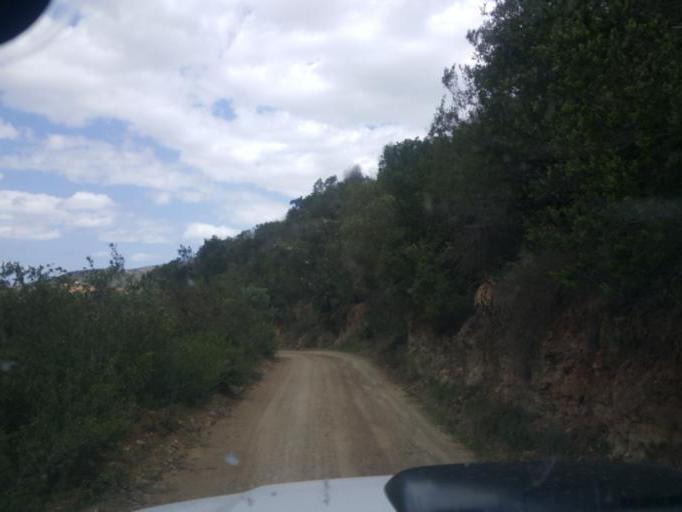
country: ZA
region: Western Cape
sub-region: Eden District Municipality
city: Knysna
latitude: -33.8182
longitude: 23.1747
